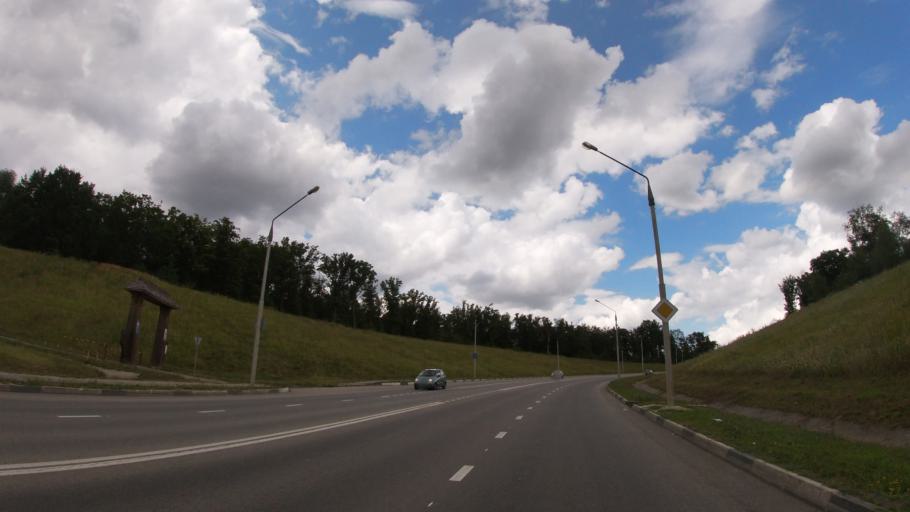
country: RU
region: Belgorod
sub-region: Belgorodskiy Rayon
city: Belgorod
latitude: 50.6227
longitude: 36.6127
